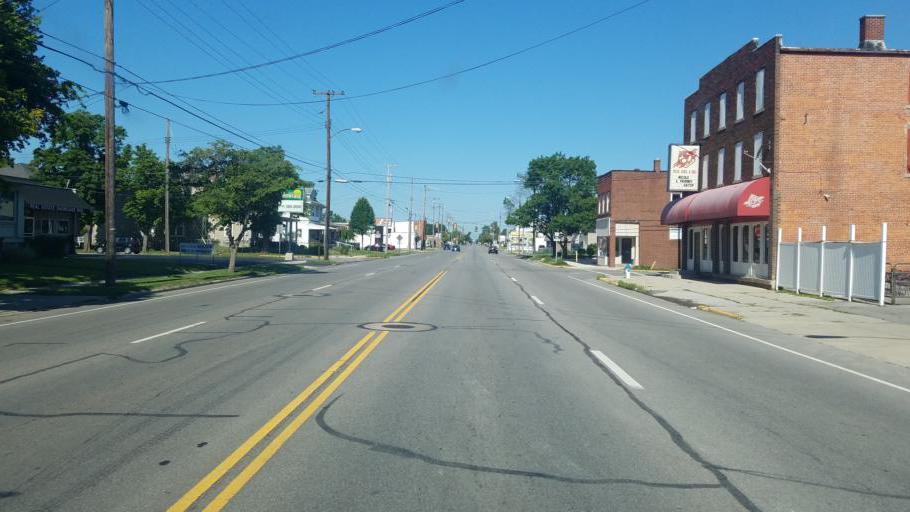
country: US
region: Ohio
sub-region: Marion County
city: Marion
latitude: 40.5894
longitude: -83.1113
